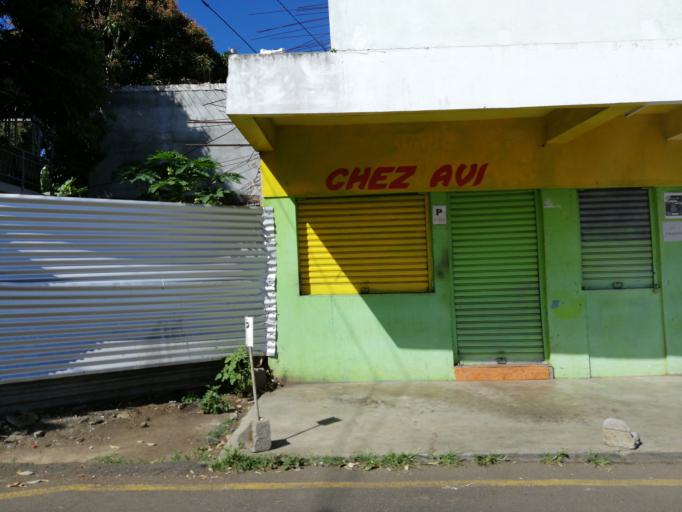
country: MU
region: Moka
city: Moka
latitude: -20.2179
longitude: 57.4674
